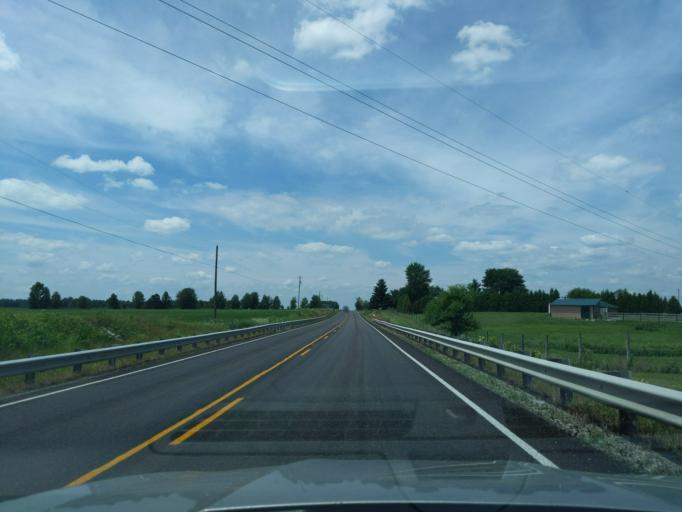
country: US
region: Indiana
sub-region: Ripley County
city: Osgood
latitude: 39.2436
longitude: -85.3478
